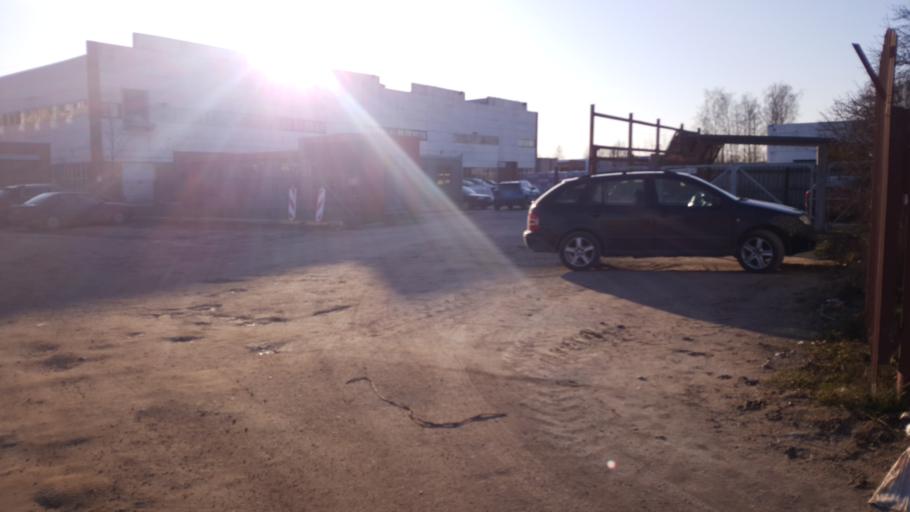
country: LT
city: Ramuciai
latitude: 54.9007
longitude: 24.0304
